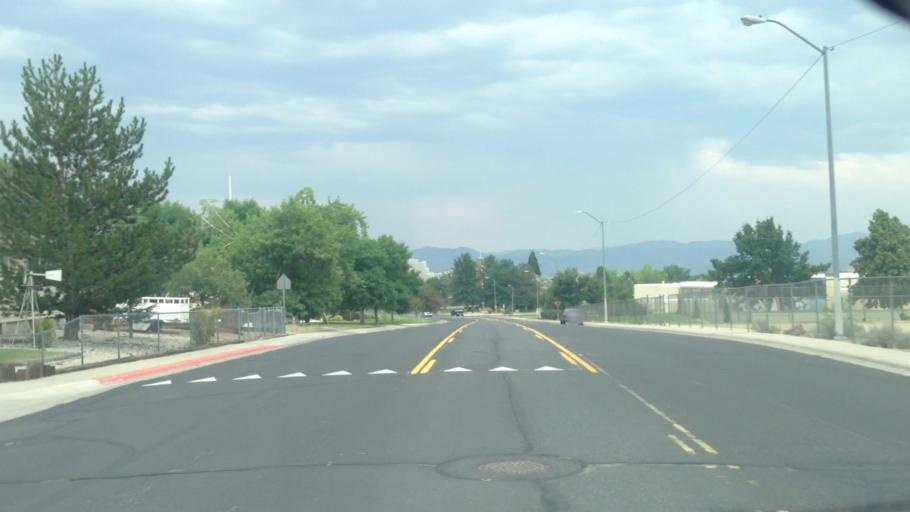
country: US
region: Nevada
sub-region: Washoe County
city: Reno
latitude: 39.5379
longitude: -119.8493
